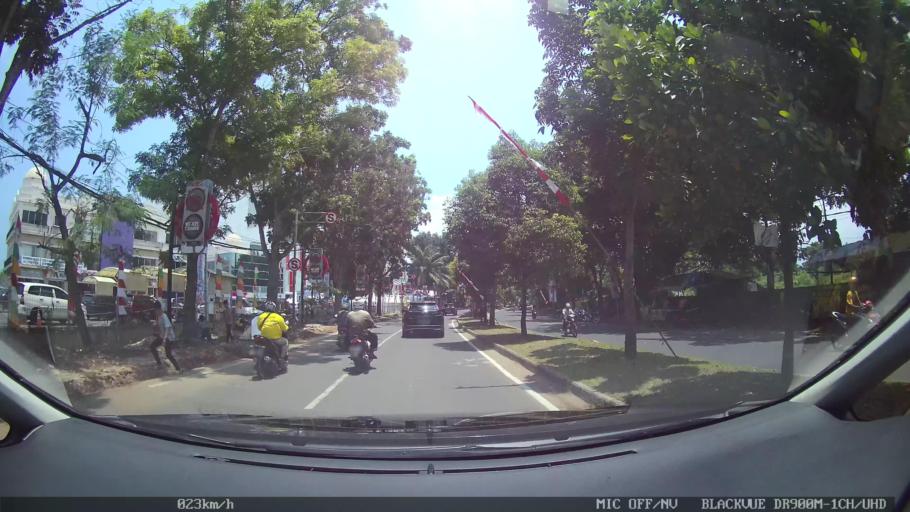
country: ID
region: Lampung
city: Kedaton
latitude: -5.3824
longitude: 105.2831
